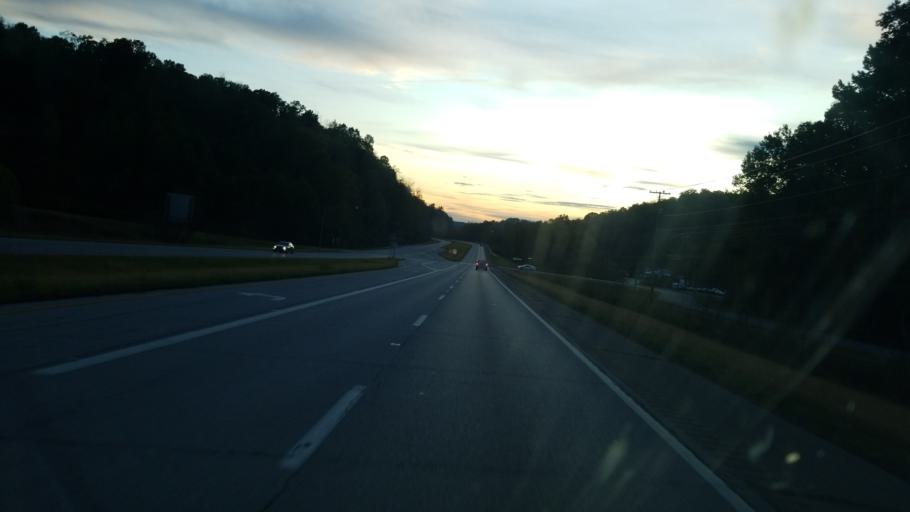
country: US
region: Ohio
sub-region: Meigs County
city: Pomeroy
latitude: 39.0569
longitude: -82.0245
